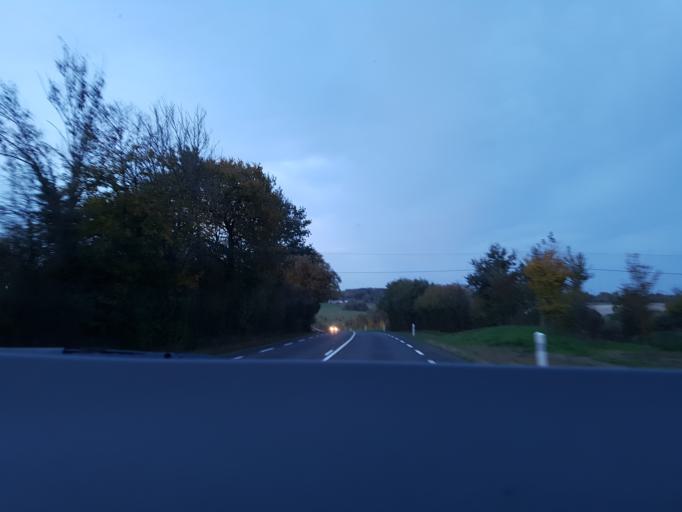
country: FR
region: Pays de la Loire
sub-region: Departement de la Mayenne
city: Montigne-le-Brillant
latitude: 48.0054
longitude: -0.8367
